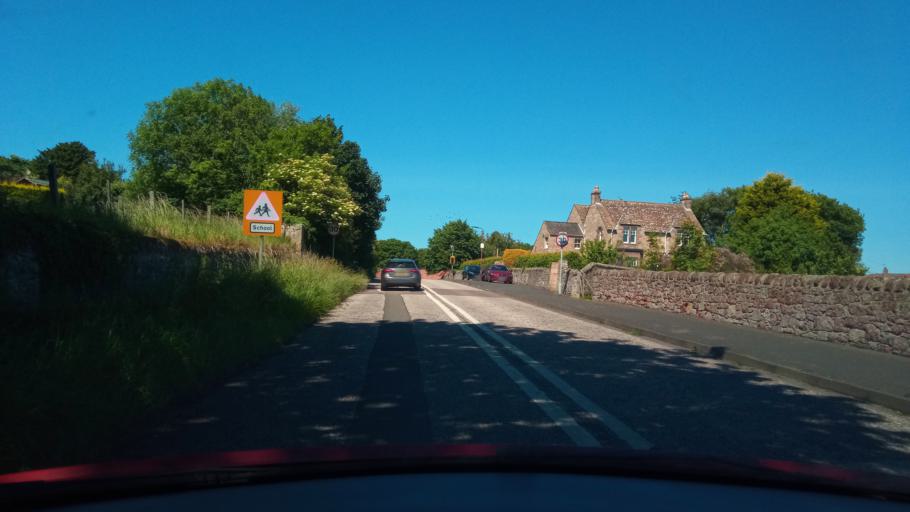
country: GB
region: Scotland
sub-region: East Lothian
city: Gullane
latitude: 56.0427
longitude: -2.7857
